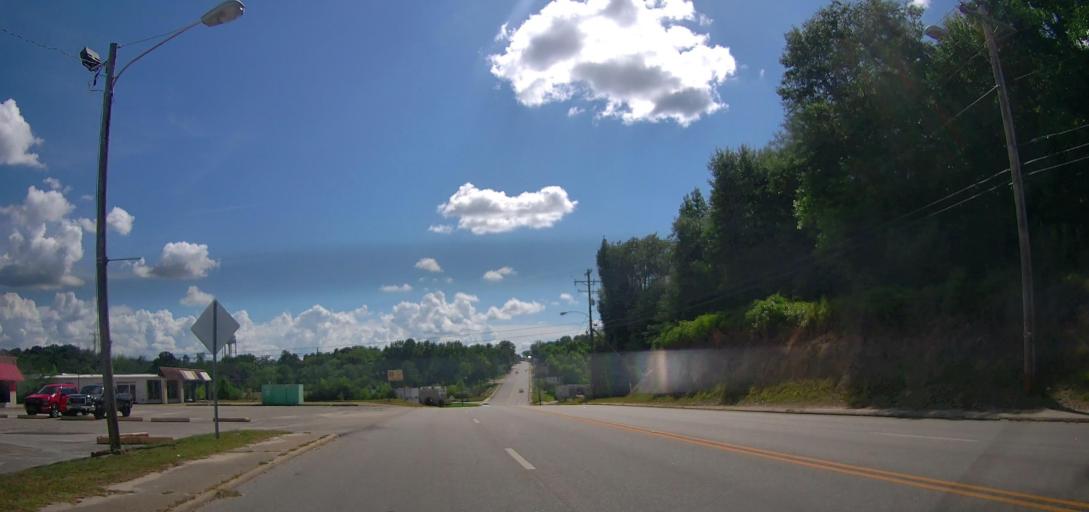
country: US
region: Alabama
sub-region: Macon County
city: Tuskegee
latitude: 32.4292
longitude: -85.6799
